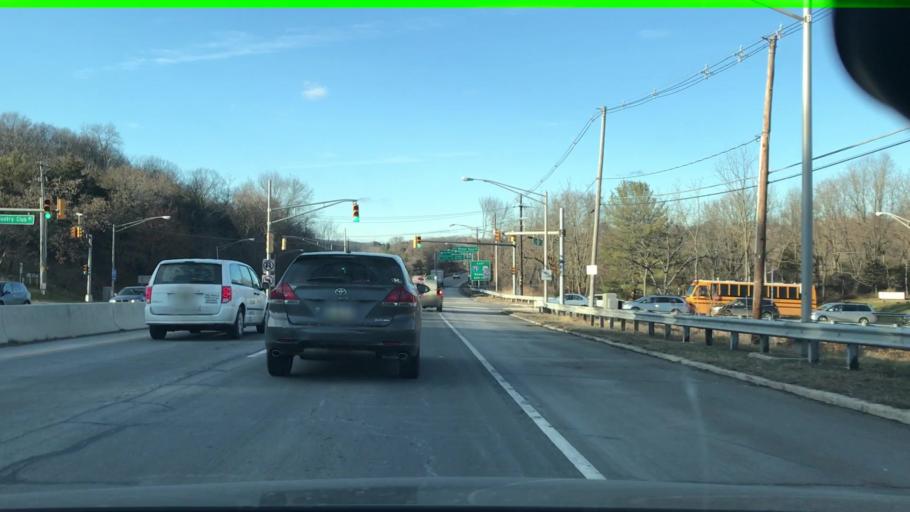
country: US
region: New Jersey
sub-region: Hunterdon County
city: Annandale
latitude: 40.6342
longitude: -74.8845
